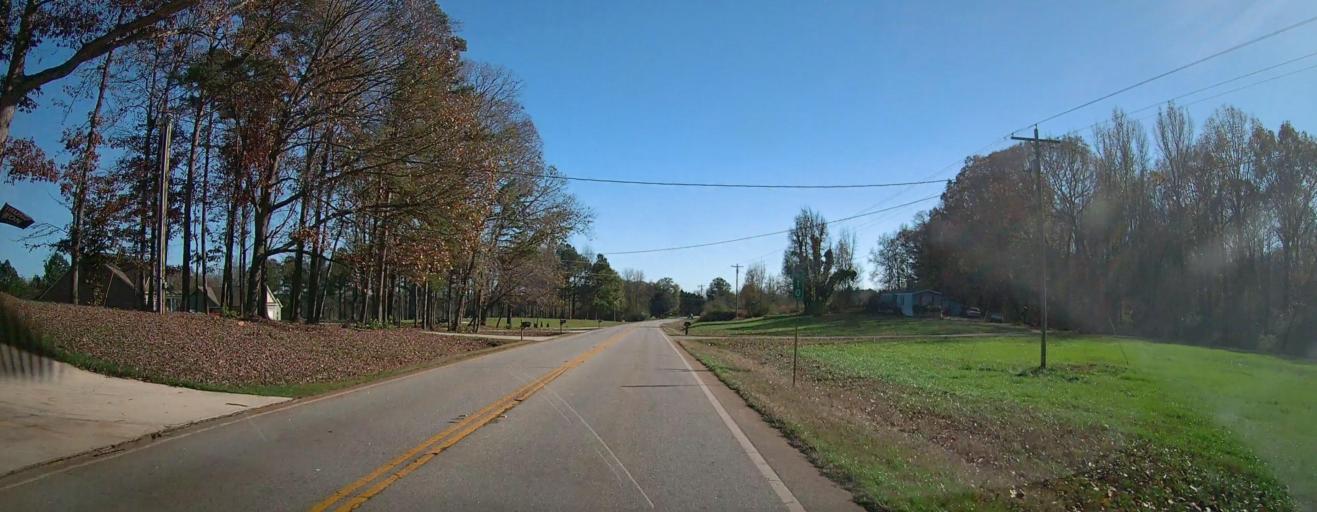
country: US
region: Georgia
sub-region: Hall County
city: Lula
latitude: 34.4547
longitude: -83.7296
